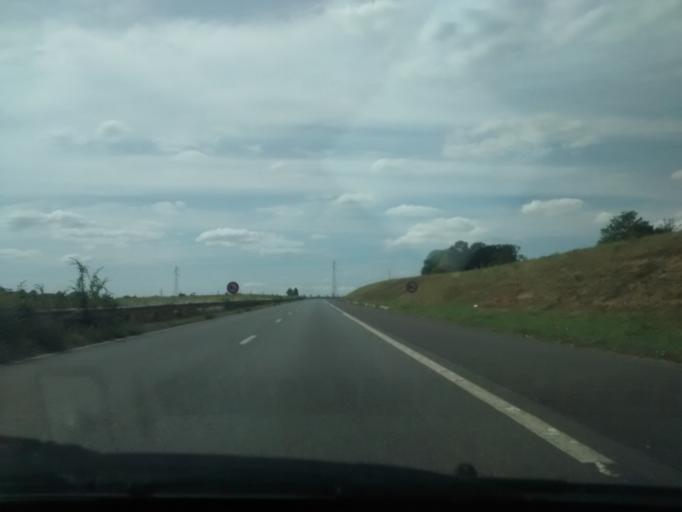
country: FR
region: Brittany
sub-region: Departement d'Ille-et-Vilaine
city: Vezin-le-Coquet
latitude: 48.1237
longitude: -1.7341
